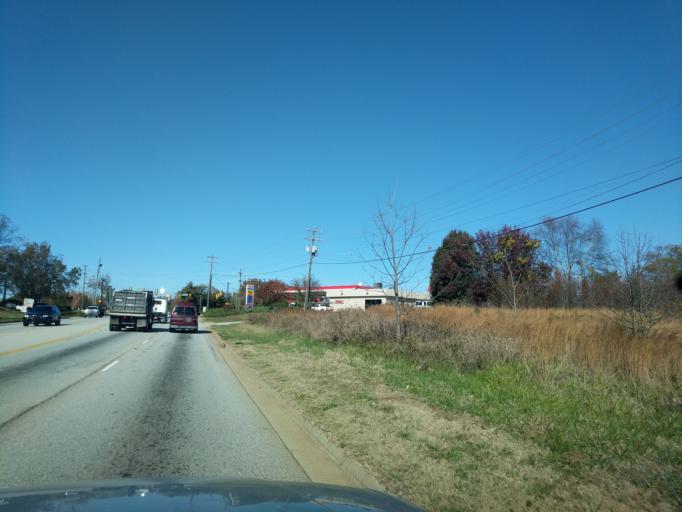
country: US
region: South Carolina
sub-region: Greenville County
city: Greer
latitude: 34.9257
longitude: -82.2441
